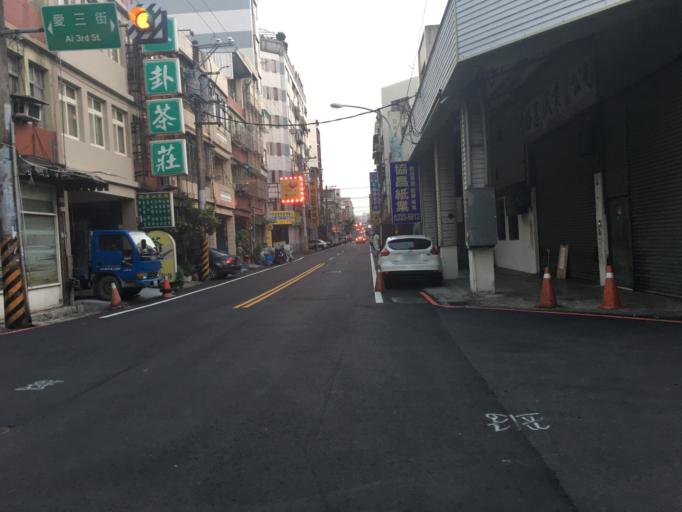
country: TW
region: Taiwan
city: Taoyuan City
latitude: 25.0045
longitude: 121.3035
